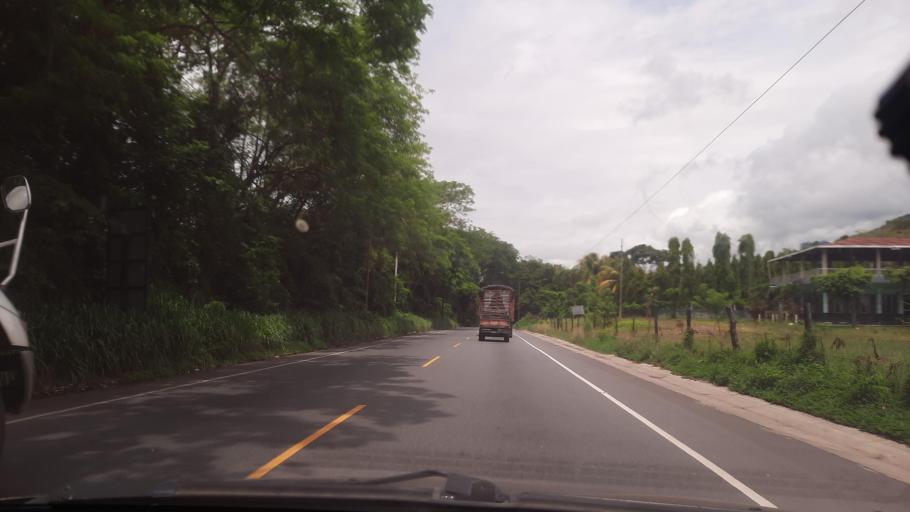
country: GT
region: Zacapa
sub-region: Municipio de Zacapa
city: Gualan
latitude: 15.1998
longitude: -89.2610
